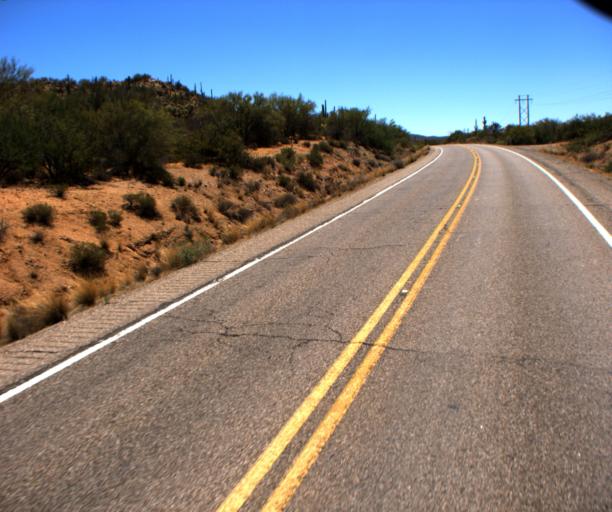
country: US
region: Arizona
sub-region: Pinal County
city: Kearny
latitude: 33.1184
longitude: -110.9716
